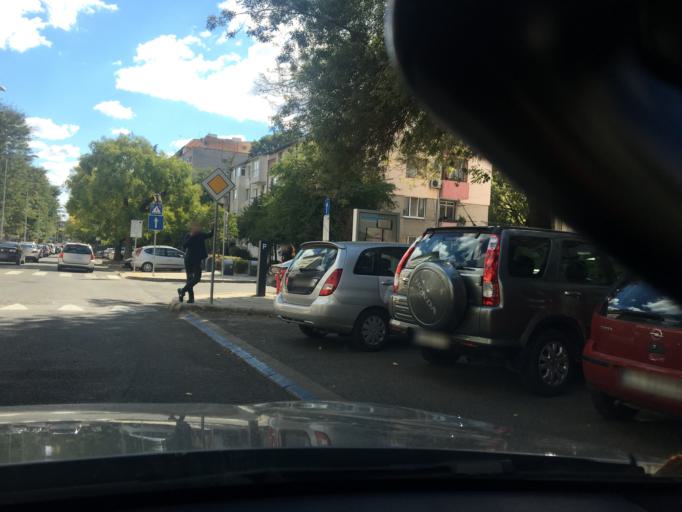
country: BG
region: Burgas
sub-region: Obshtina Burgas
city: Burgas
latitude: 42.5007
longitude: 27.4710
